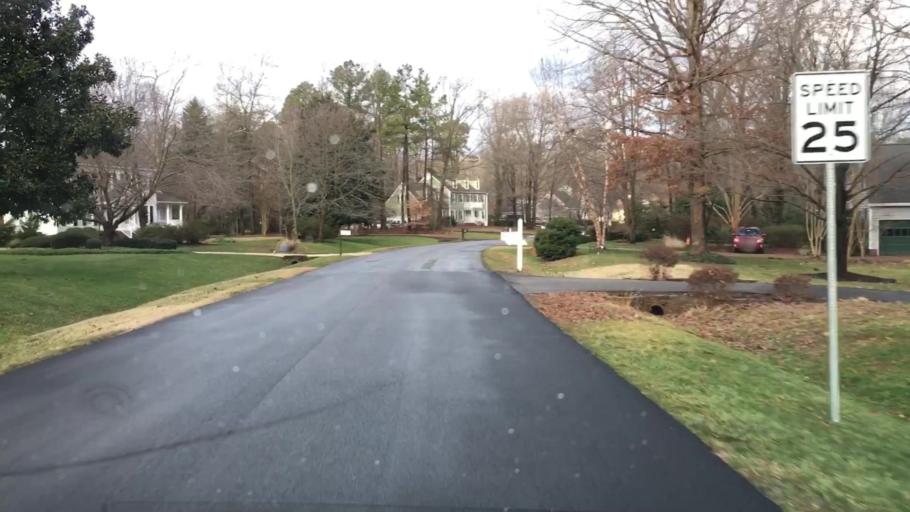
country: US
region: Virginia
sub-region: Chesterfield County
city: Bon Air
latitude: 37.5296
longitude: -77.6033
